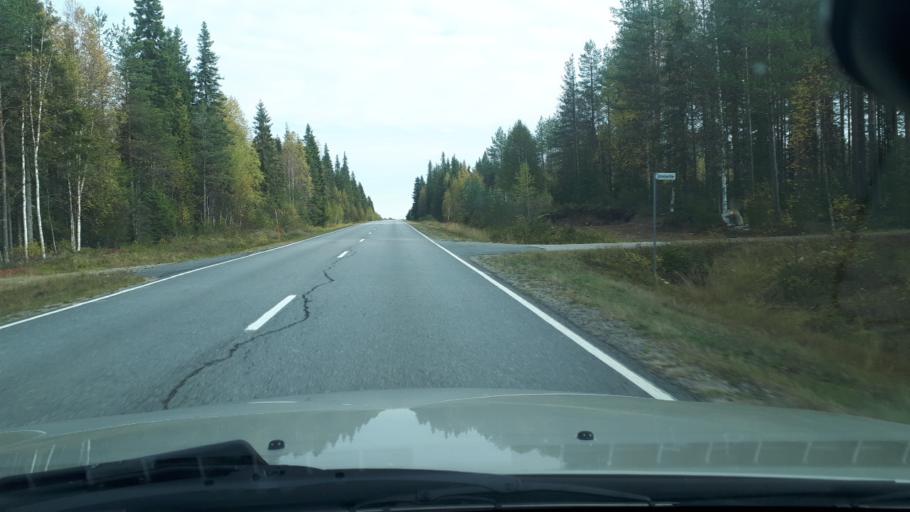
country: FI
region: Lapland
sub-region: Rovaniemi
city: Ranua
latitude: 65.9738
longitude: 26.1101
